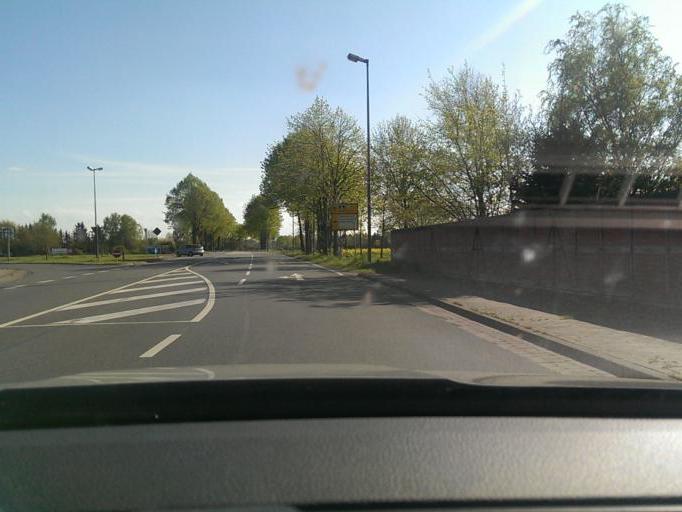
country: DE
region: Lower Saxony
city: Langenhagen
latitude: 52.4718
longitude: 9.7331
